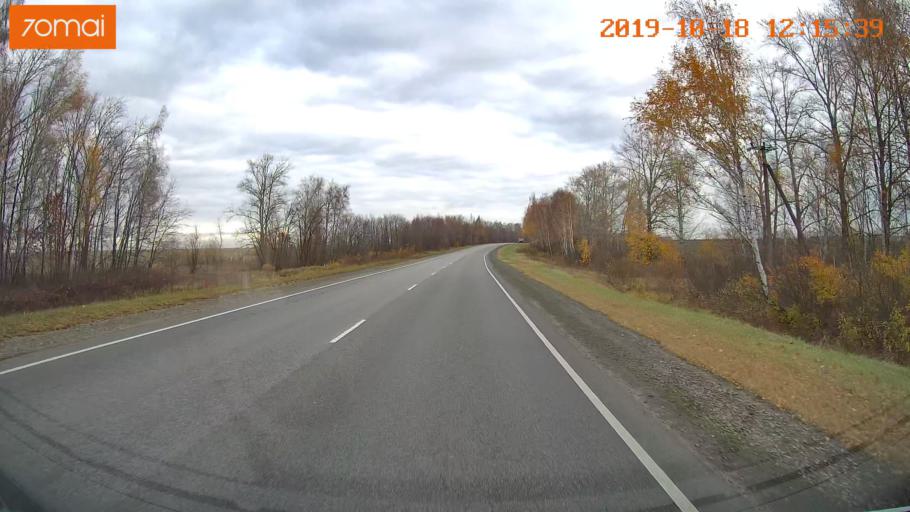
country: RU
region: Rjazan
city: Zakharovo
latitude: 54.4465
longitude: 39.4040
